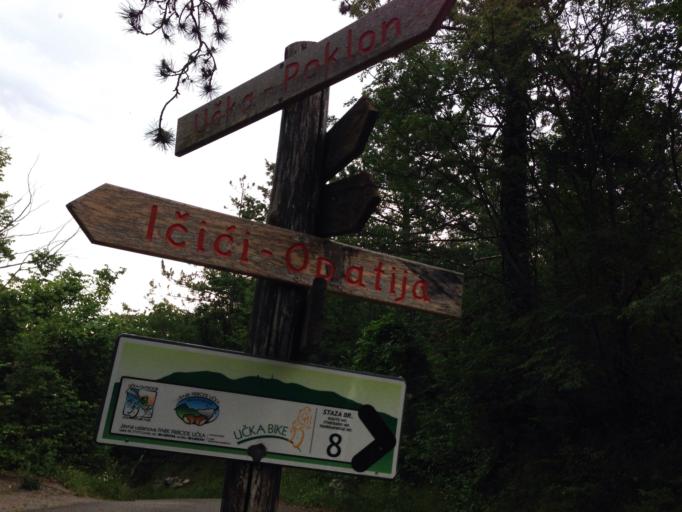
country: HR
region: Istarska
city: Lovran
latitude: 45.3104
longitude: 14.2538
